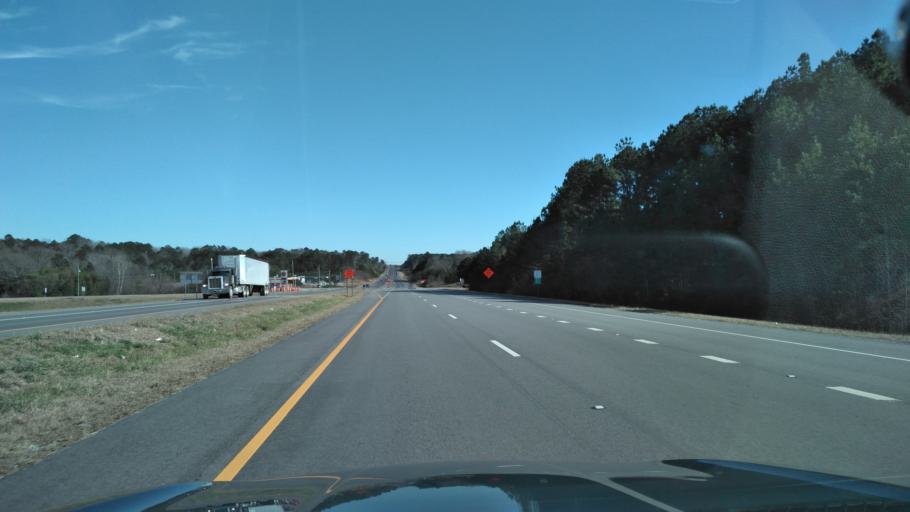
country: US
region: Alabama
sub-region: Walker County
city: Jasper
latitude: 33.8551
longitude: -87.3400
